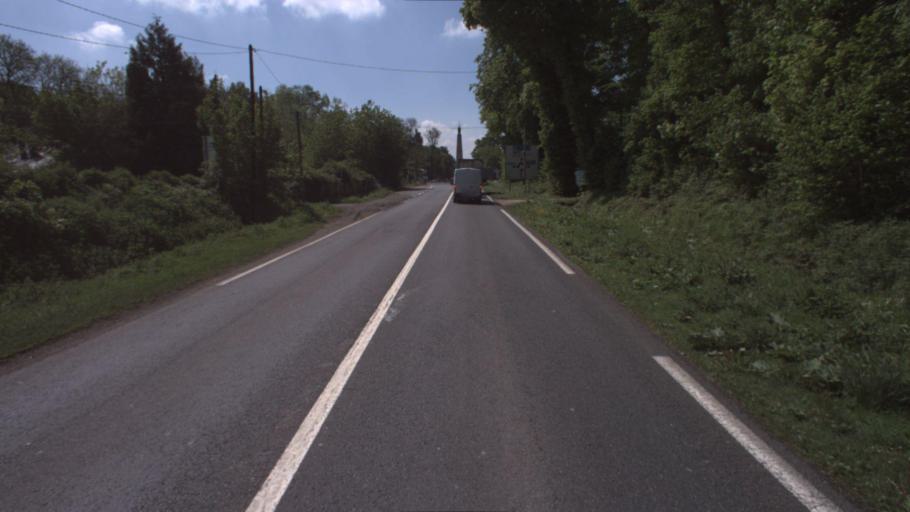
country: FR
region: Ile-de-France
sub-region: Departement de Seine-et-Marne
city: La Houssaye-en-Brie
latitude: 48.7931
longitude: 2.8696
